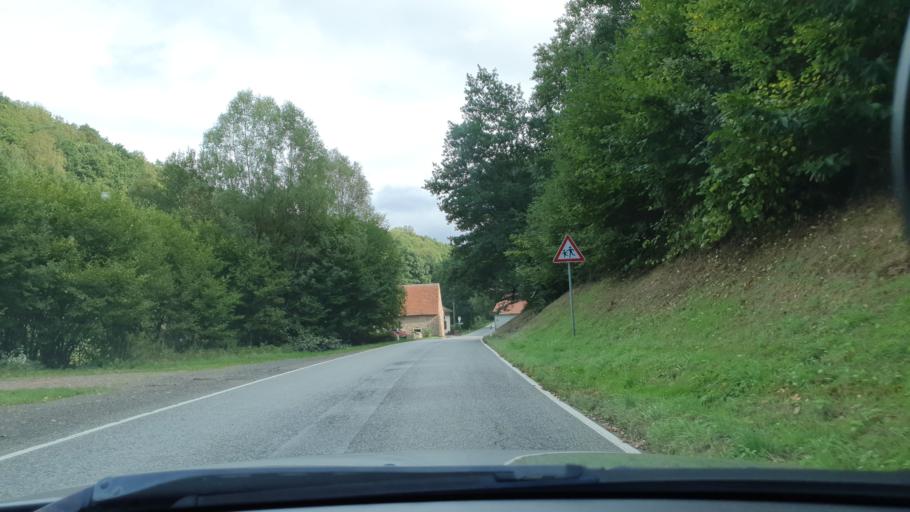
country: DE
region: Rheinland-Pfalz
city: Gerhardsbrunn
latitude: 49.3459
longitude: 7.5111
